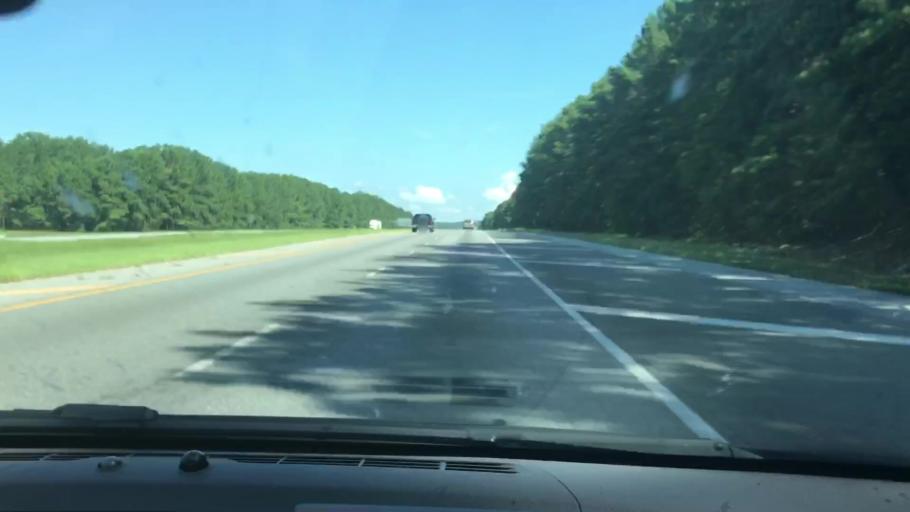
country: US
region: Alabama
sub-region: Russell County
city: Phenix City
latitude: 32.5678
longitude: -84.9619
